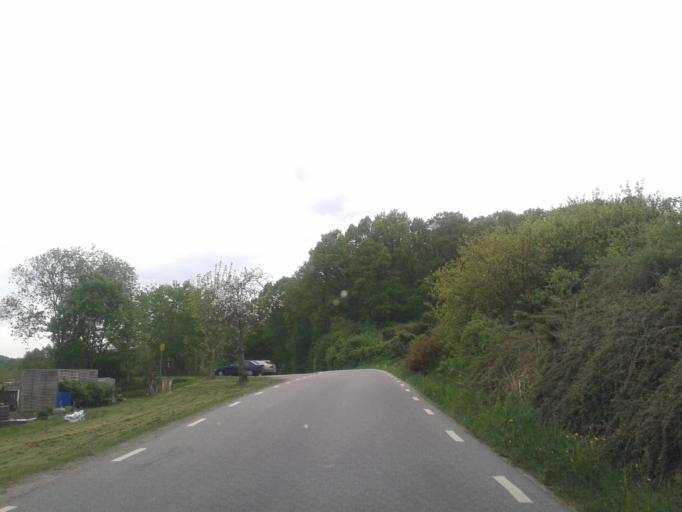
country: SE
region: Vaestra Goetaland
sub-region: Kungalvs Kommun
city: Kungalv
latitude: 57.8637
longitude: 11.9564
